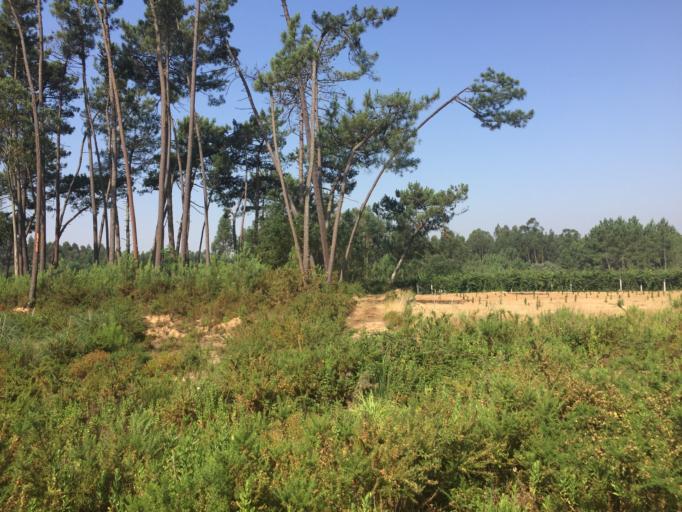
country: PT
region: Coimbra
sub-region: Cantanhede
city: Cantanhede
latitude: 40.4254
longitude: -8.5452
